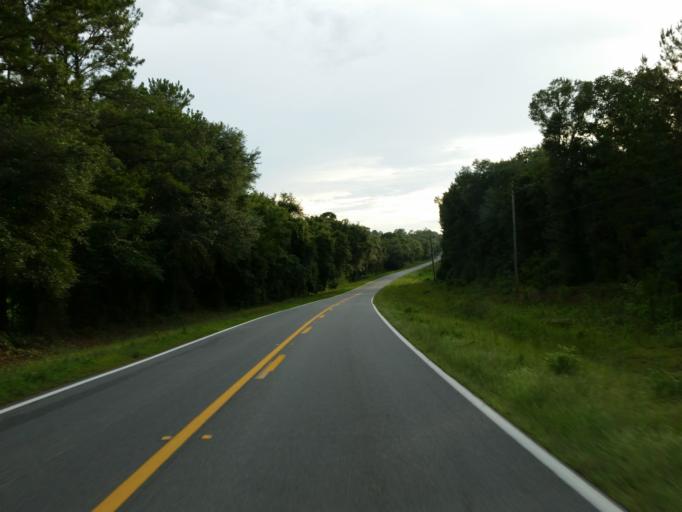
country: US
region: Florida
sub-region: Alachua County
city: High Springs
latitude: 29.9527
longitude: -82.5932
